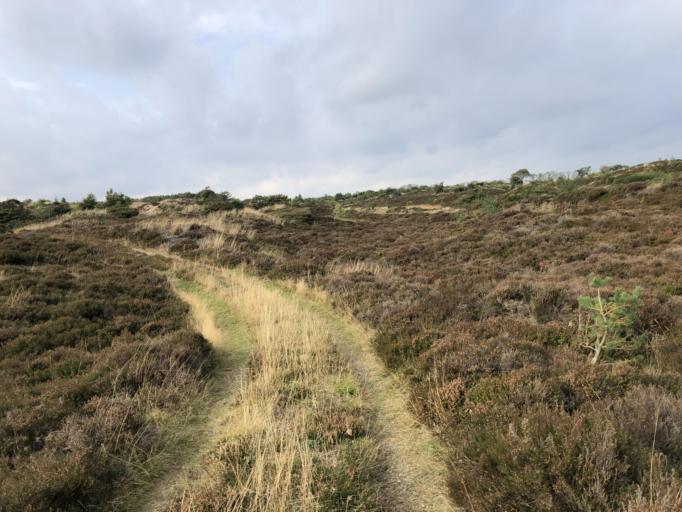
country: DK
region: Central Jutland
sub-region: Holstebro Kommune
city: Ulfborg
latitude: 56.2130
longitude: 8.4332
